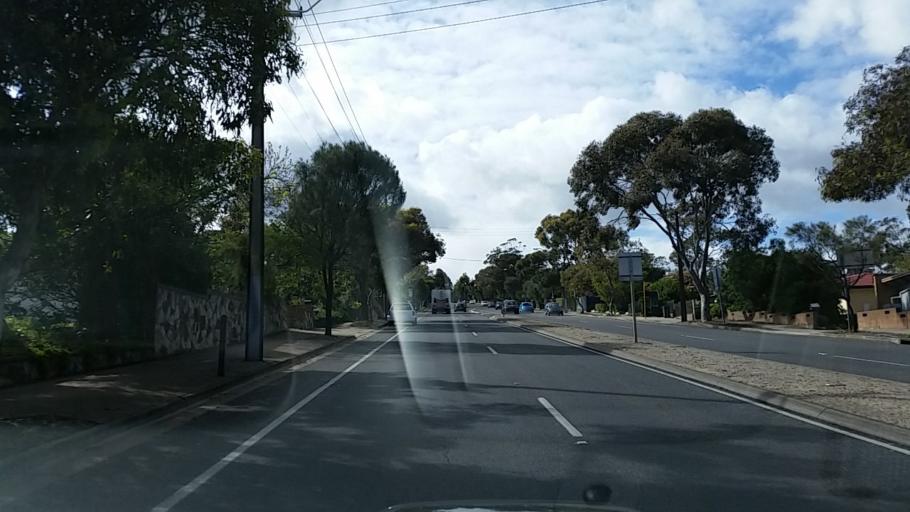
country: AU
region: South Australia
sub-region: Marion
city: Marion
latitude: -35.0192
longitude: 138.5803
